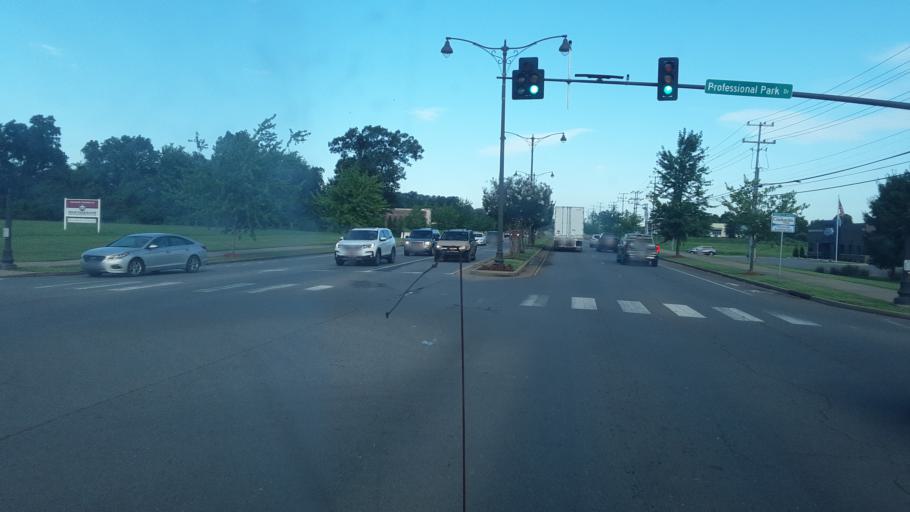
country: US
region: Tennessee
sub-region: Montgomery County
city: Clarksville
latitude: 36.5799
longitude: -87.2718
